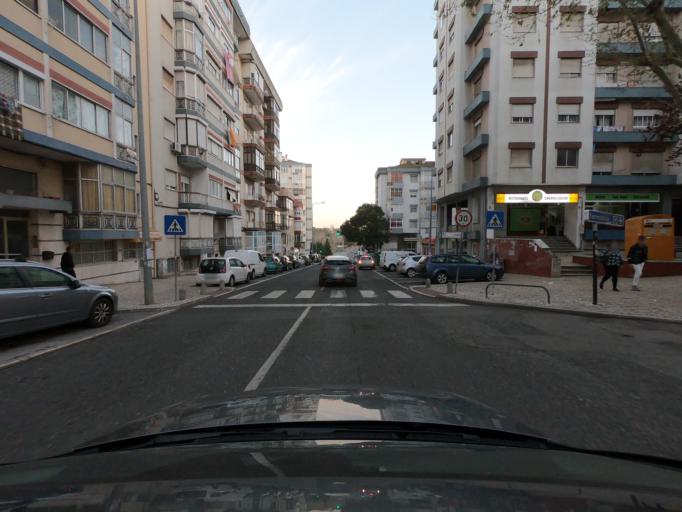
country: PT
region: Lisbon
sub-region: Sintra
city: Queluz
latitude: 38.7574
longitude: -9.2676
